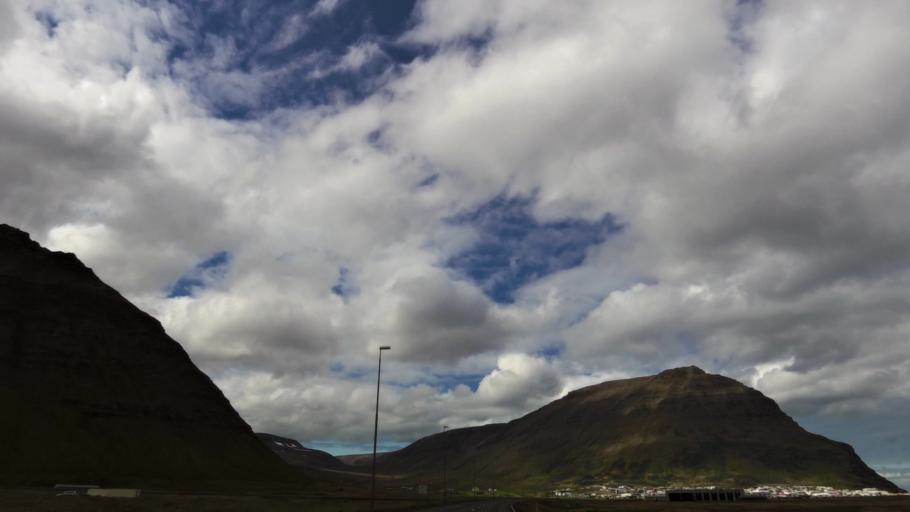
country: IS
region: Westfjords
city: Isafjoerdur
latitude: 66.1461
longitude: -23.2374
